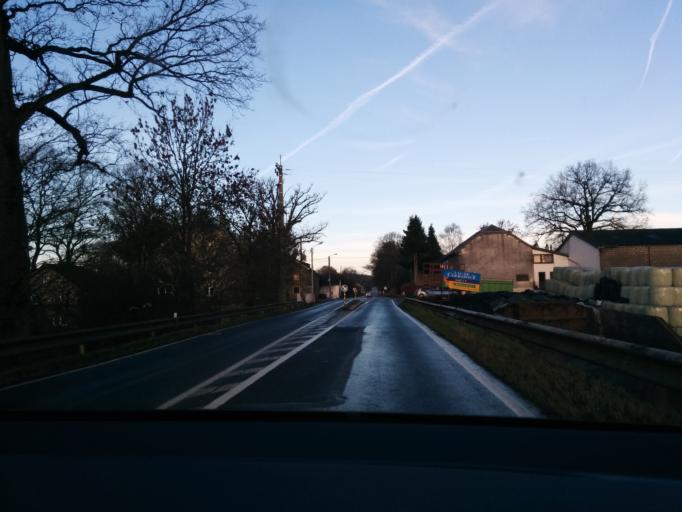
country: BE
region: Wallonia
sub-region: Province du Luxembourg
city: Gouvy
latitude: 50.1944
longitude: 6.0085
